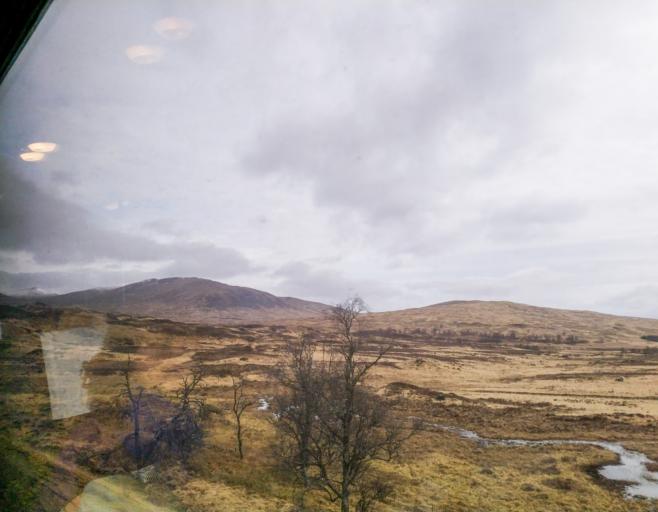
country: GB
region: Scotland
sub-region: Highland
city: Spean Bridge
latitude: 56.6882
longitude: -4.5764
